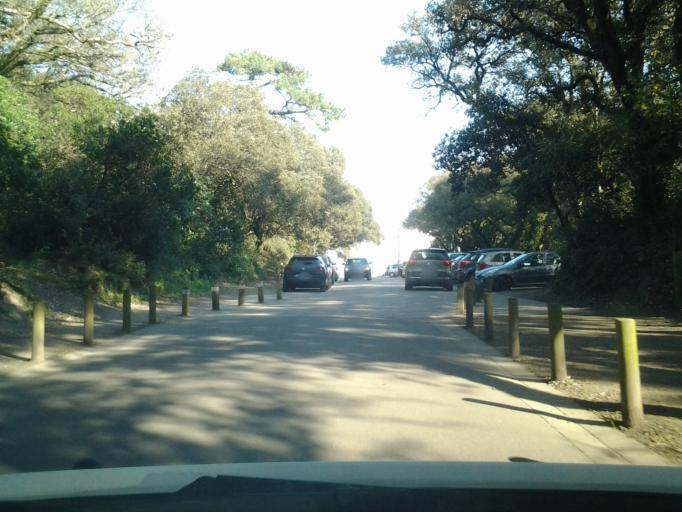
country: FR
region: Pays de la Loire
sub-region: Departement de la Vendee
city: La Gueriniere
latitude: 47.0095
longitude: -2.2230
